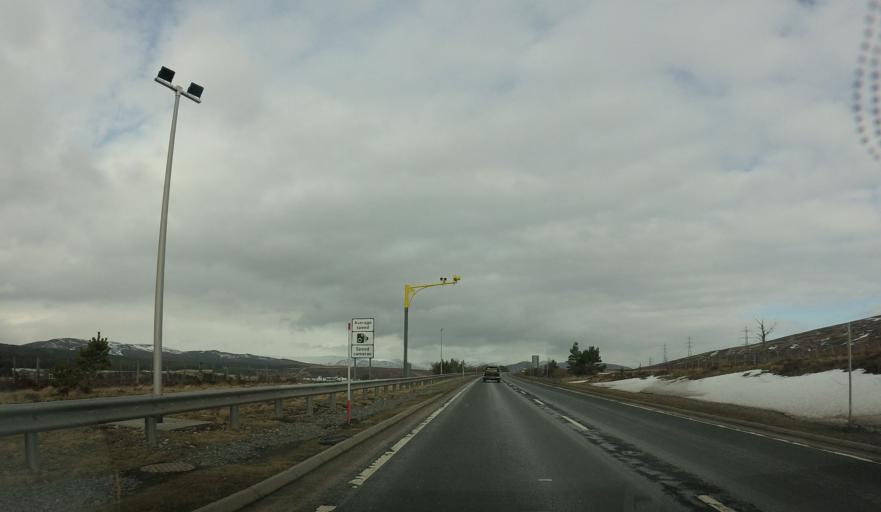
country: GB
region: Scotland
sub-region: Highland
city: Kingussie
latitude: 56.9287
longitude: -4.2358
